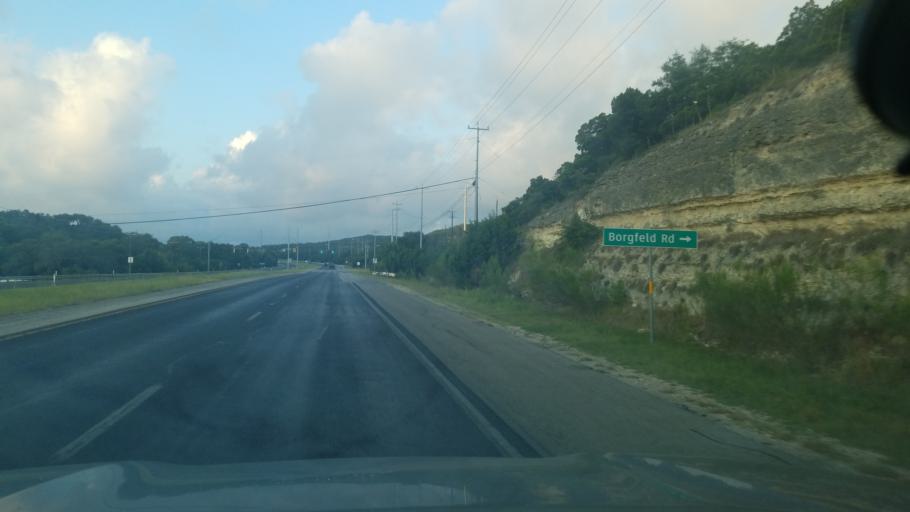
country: US
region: Texas
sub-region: Bexar County
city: Timberwood Park
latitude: 29.7123
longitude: -98.4481
